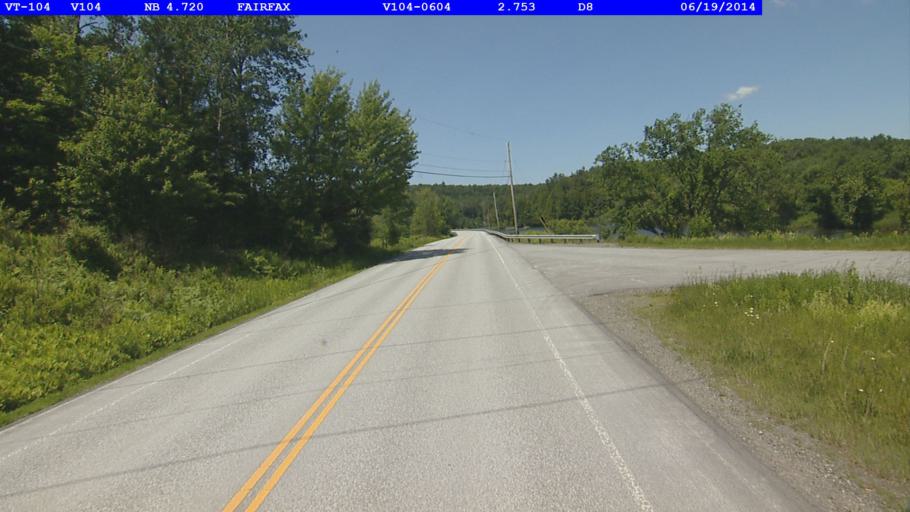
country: US
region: Vermont
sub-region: Chittenden County
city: Milton
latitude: 44.6460
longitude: -72.9779
